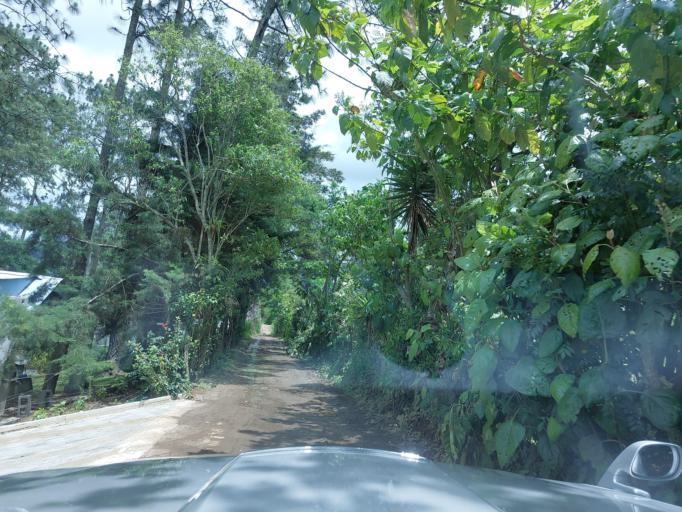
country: GT
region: Chimaltenango
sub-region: Municipio de Chimaltenango
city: Chimaltenango
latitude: 14.6423
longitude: -90.8291
